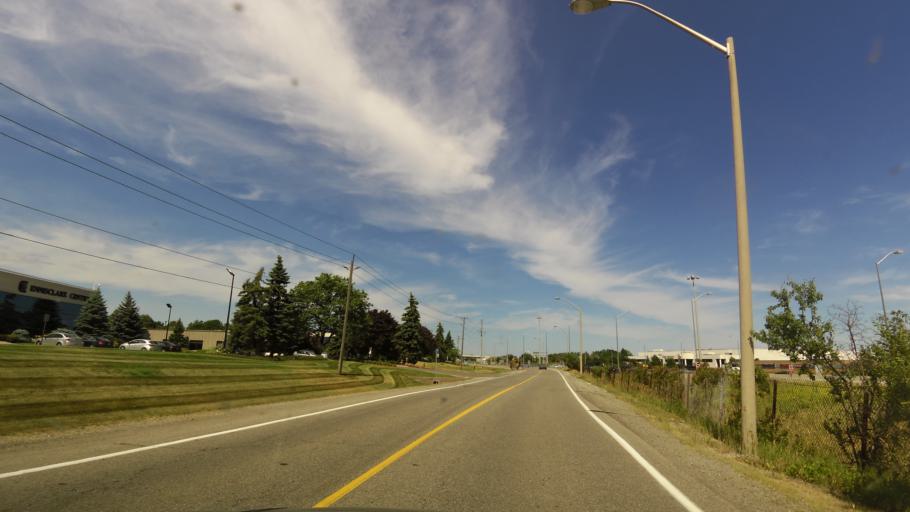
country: CA
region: Ontario
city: Oakville
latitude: 43.4354
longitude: -79.7141
